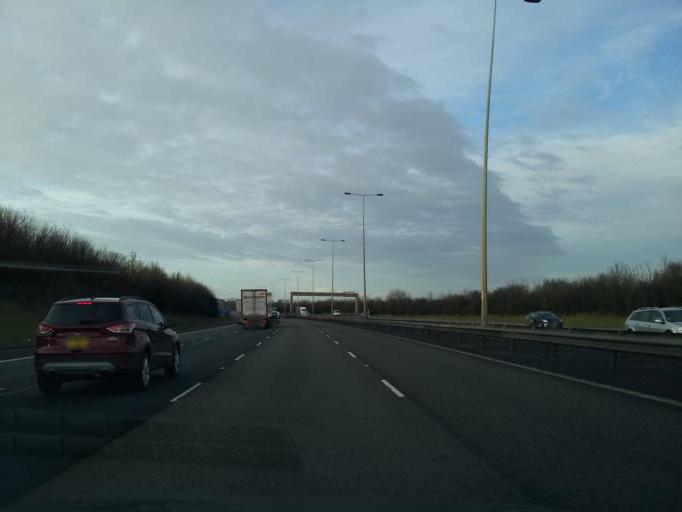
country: GB
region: England
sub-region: Cambridgeshire
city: Stilton
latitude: 52.4856
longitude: -0.2854
